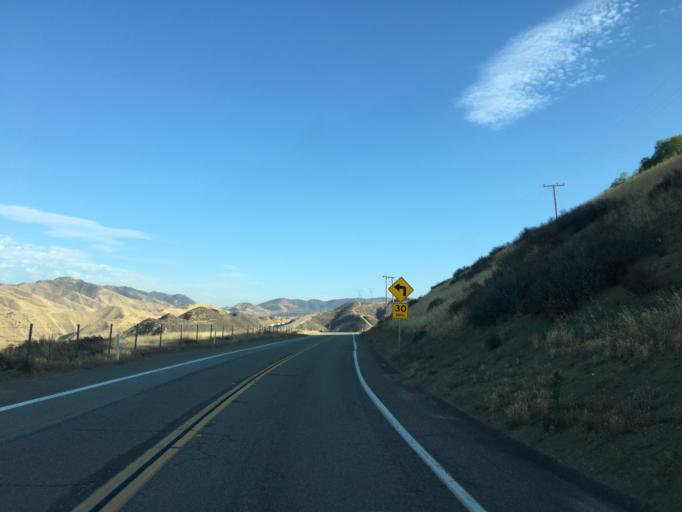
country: US
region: California
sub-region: Los Angeles County
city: Castaic
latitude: 34.5175
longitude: -118.6357
